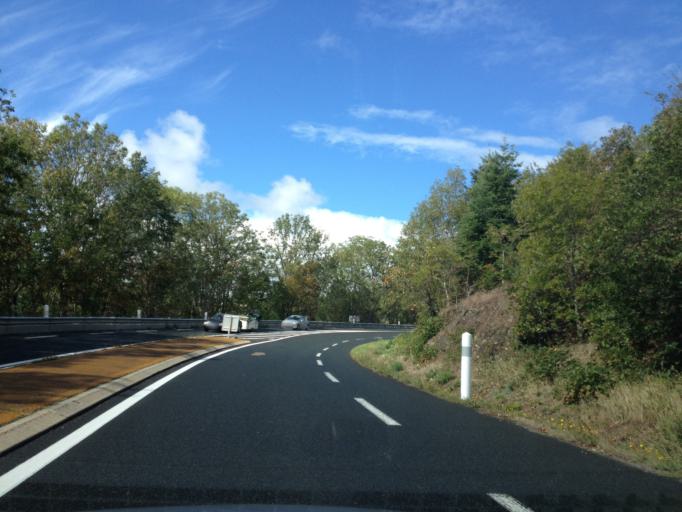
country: FR
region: Rhone-Alpes
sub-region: Departement de la Loire
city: Violay
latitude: 45.9088
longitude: 4.3573
